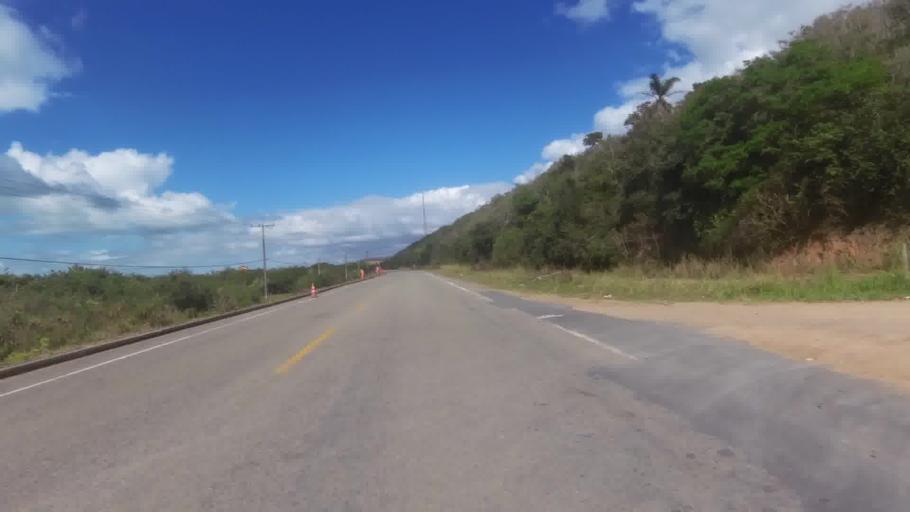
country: BR
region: Espirito Santo
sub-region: Marataizes
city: Marataizes
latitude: -21.1767
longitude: -40.9204
